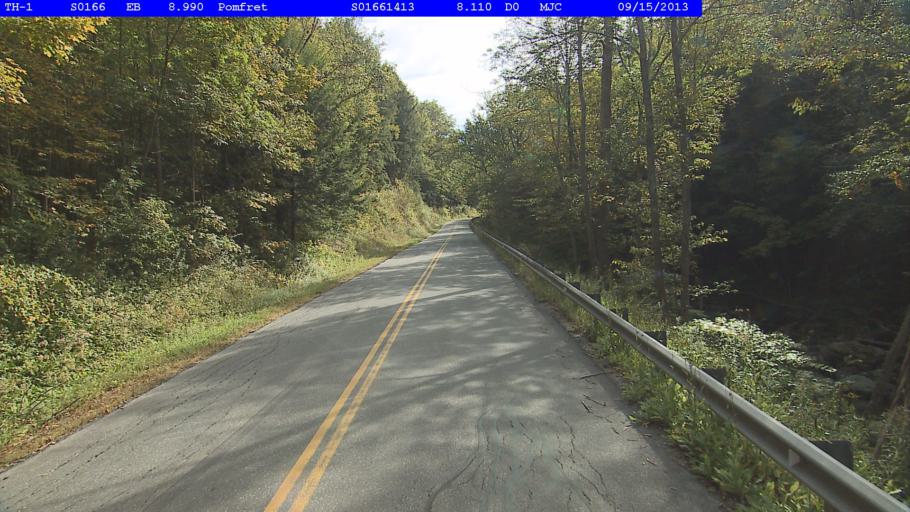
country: US
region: Vermont
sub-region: Windsor County
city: Woodstock
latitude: 43.7238
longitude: -72.4614
